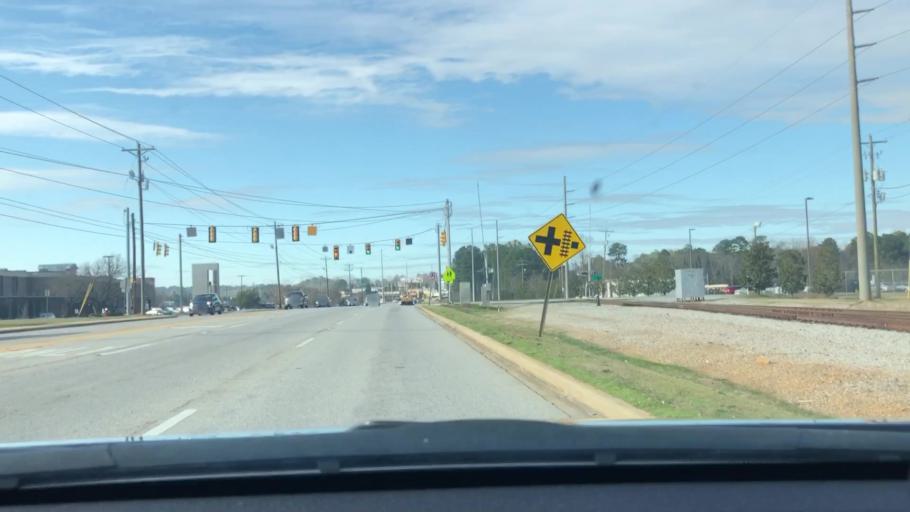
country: US
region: South Carolina
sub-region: Lexington County
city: Irmo
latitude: 34.0684
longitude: -81.1717
